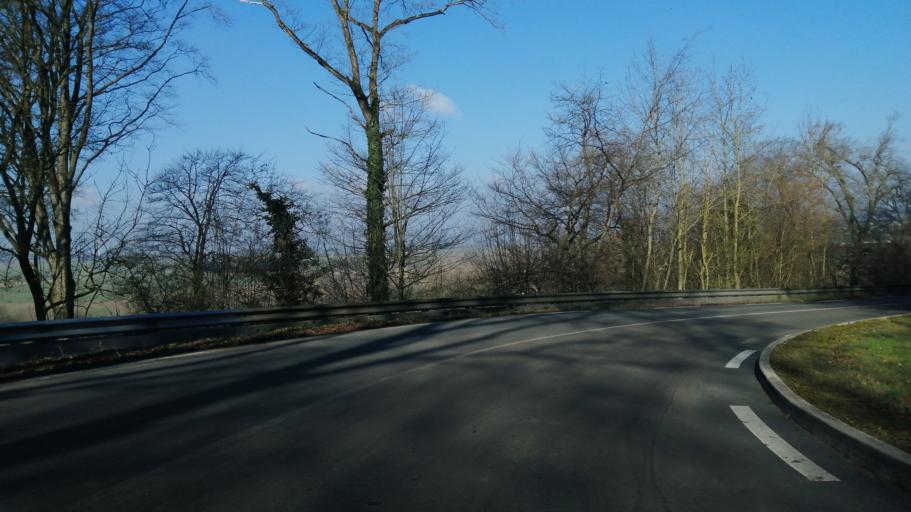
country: FR
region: Nord-Pas-de-Calais
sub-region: Departement du Pas-de-Calais
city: Ranchicourt
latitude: 50.4079
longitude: 2.5872
